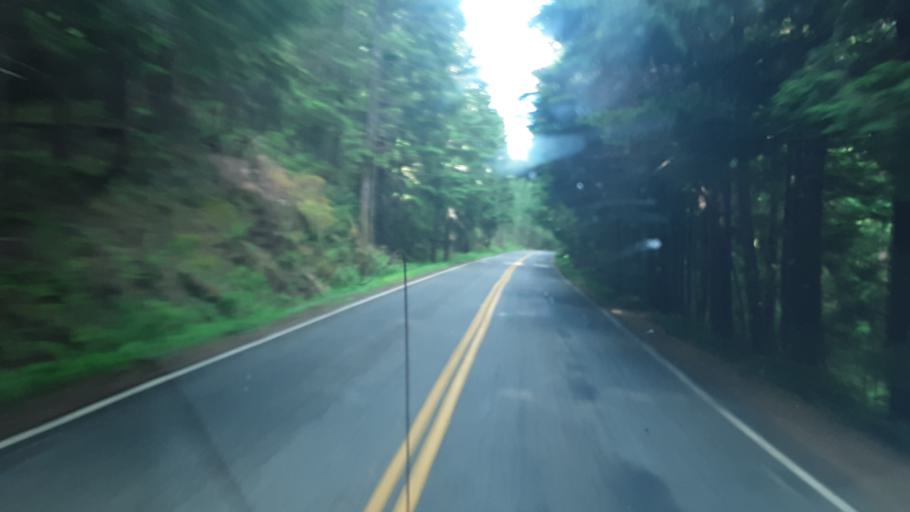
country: US
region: Washington
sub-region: Pierce County
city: Buckley
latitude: 46.7592
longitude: -121.5530
